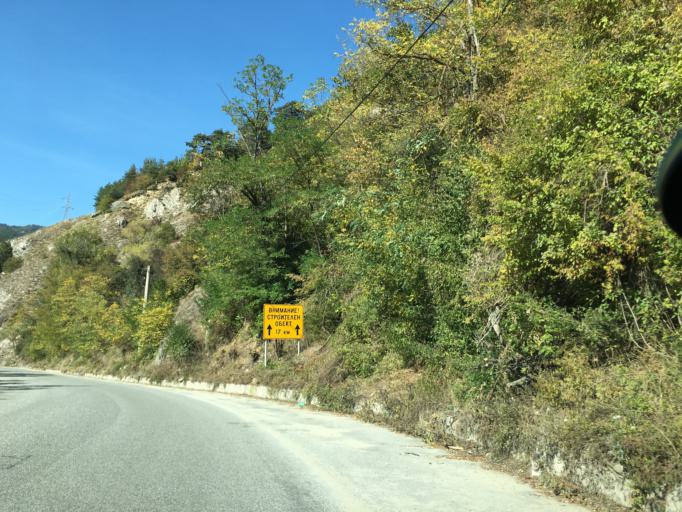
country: BG
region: Smolyan
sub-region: Obshtina Devin
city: Devin
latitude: 41.7342
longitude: 24.4240
